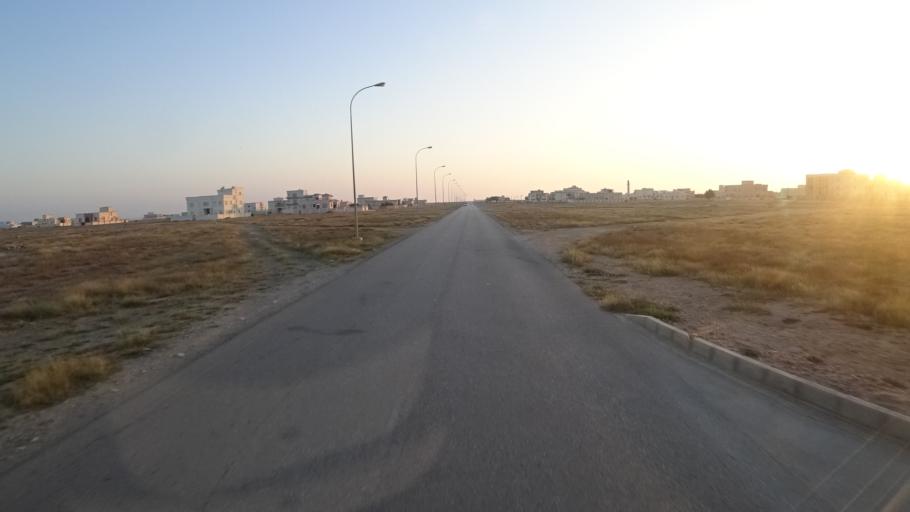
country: OM
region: Zufar
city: Salalah
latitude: 16.9854
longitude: 54.7132
